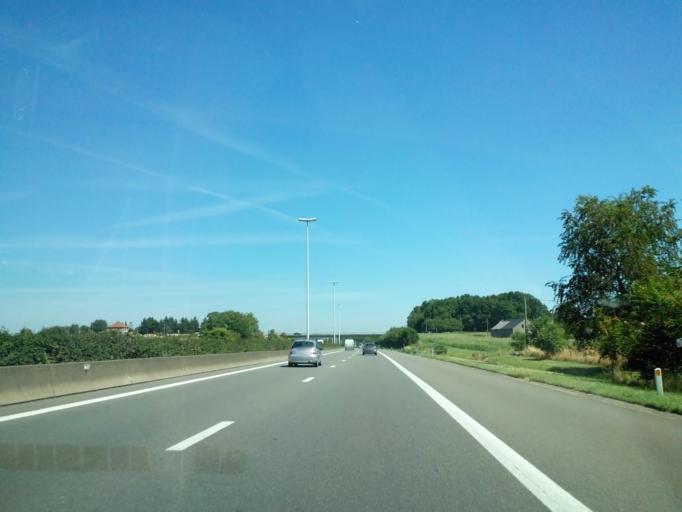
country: BE
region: Flanders
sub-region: Provincie Vlaams-Brabant
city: Bekkevoort
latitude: 50.9553
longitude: 4.9570
